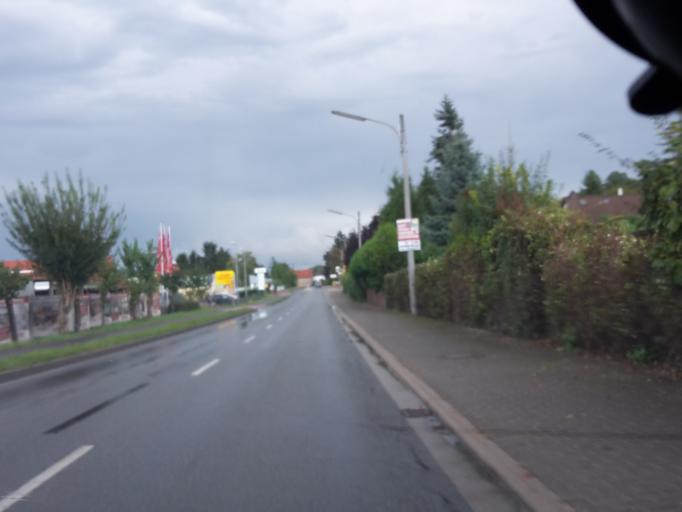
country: DE
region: Rheinland-Pfalz
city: Nackenheim
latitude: 49.9204
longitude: 8.3320
